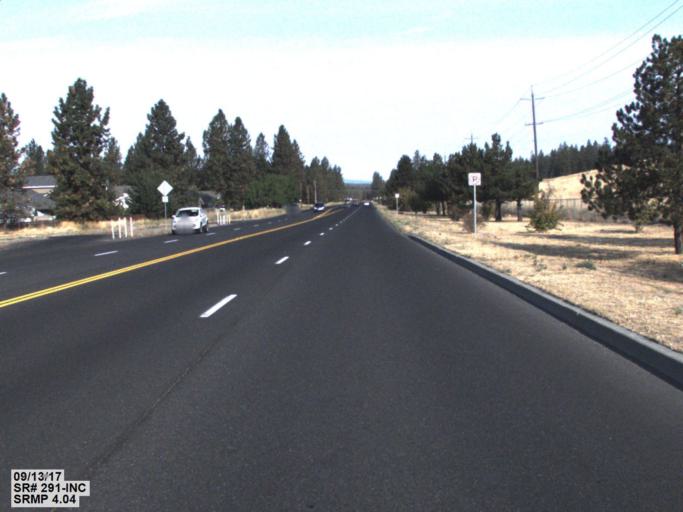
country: US
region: Washington
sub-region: Spokane County
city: Town and Country
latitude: 47.7239
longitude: -117.4927
